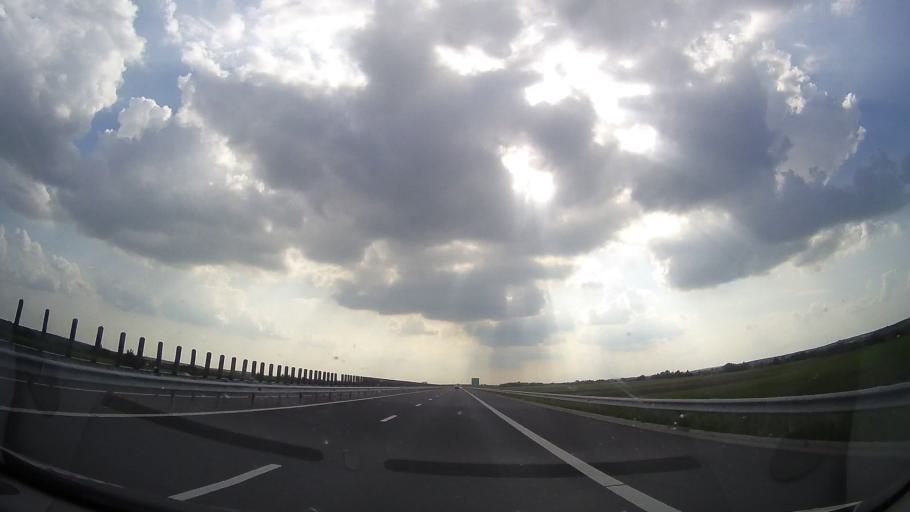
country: RO
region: Timis
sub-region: Comuna Balint
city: Balint
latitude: 45.8036
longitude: 21.8949
